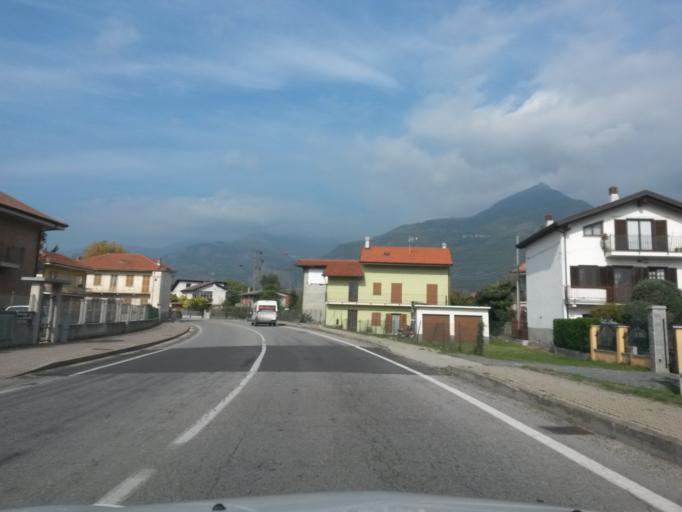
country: IT
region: Piedmont
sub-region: Provincia di Torino
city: Sant'Ambrogio di Torino
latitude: 45.0987
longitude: 7.3655
